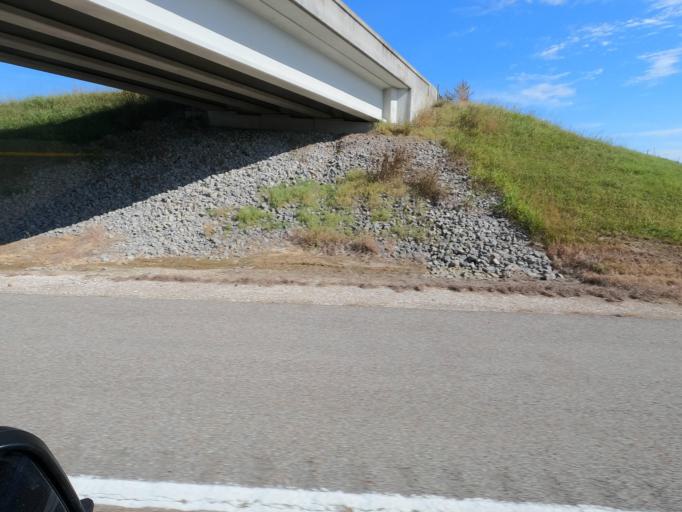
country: US
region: Tennessee
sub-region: Crockett County
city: Alamo
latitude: 35.8120
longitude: -89.1608
